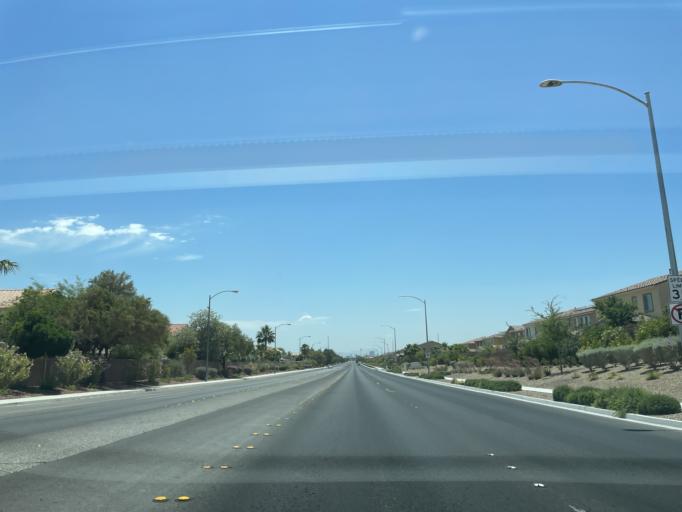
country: US
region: Nevada
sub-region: Clark County
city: North Las Vegas
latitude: 36.2829
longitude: -115.1532
